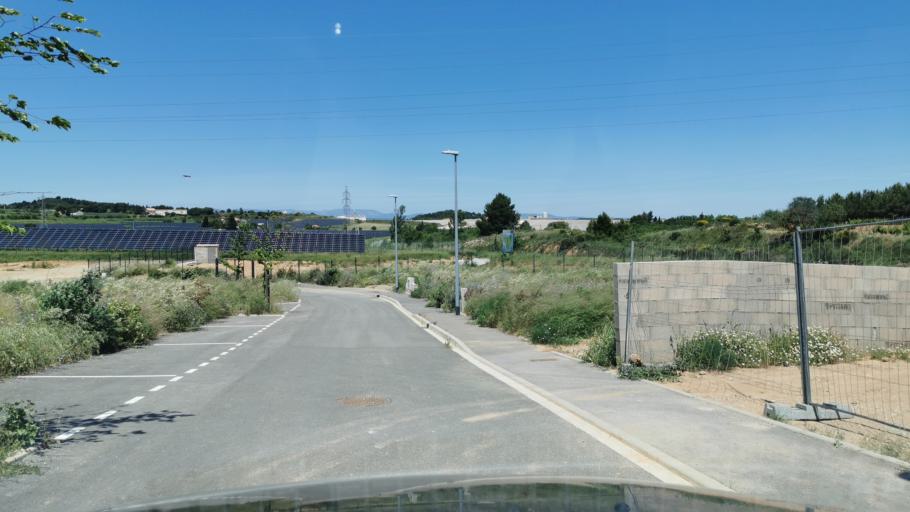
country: FR
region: Languedoc-Roussillon
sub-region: Departement de l'Aude
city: Narbonne
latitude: 43.2019
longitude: 2.9803
